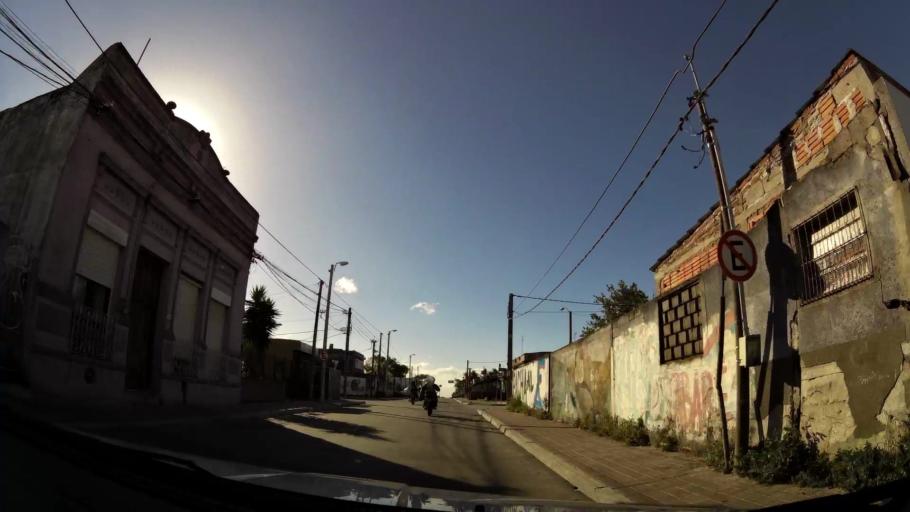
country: UY
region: Montevideo
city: Montevideo
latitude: -34.8442
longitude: -56.2394
